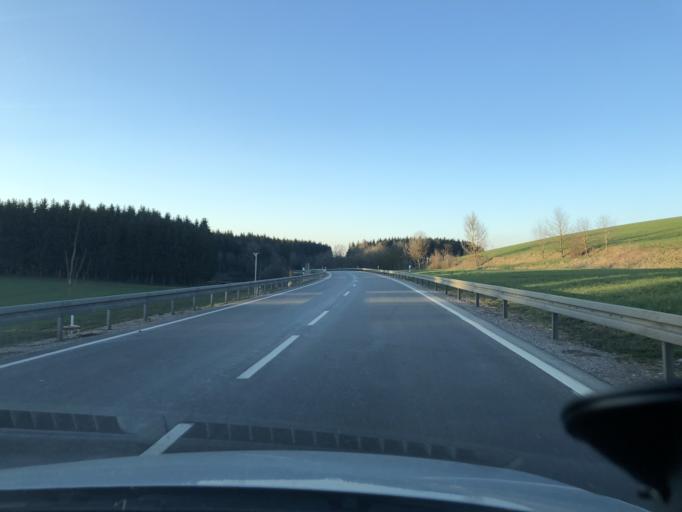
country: DE
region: Baden-Wuerttemberg
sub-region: Freiburg Region
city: Hufingen
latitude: 47.8990
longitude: 8.5088
